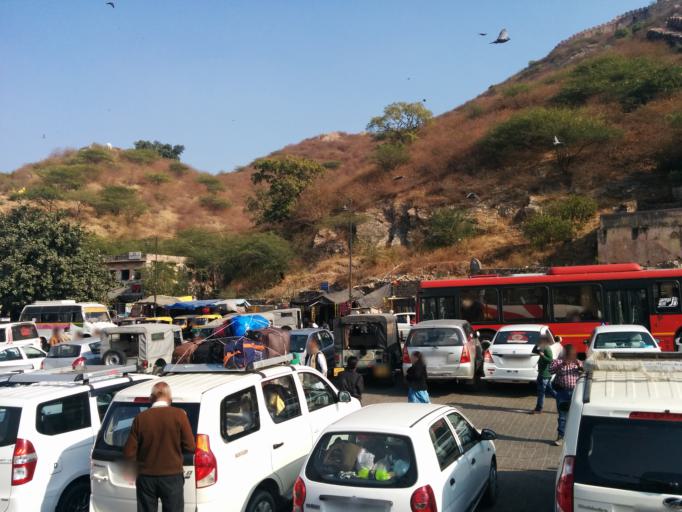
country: IN
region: Rajasthan
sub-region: Jaipur
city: Jaipur
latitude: 26.9853
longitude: 75.8538
